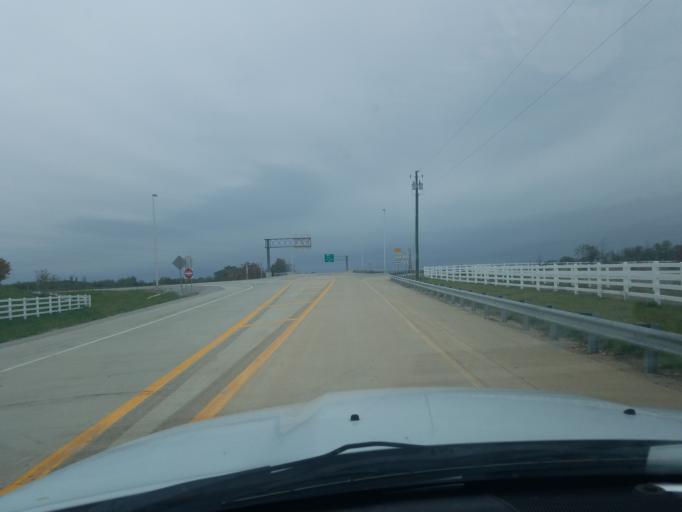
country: US
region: Kentucky
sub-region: Jefferson County
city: Prospect
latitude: 38.3478
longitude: -85.6667
